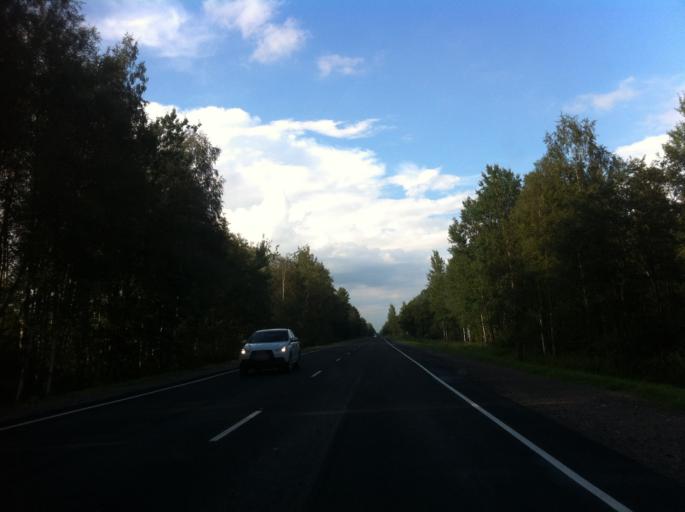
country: RU
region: Leningrad
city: Luga
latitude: 58.4641
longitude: 29.7658
